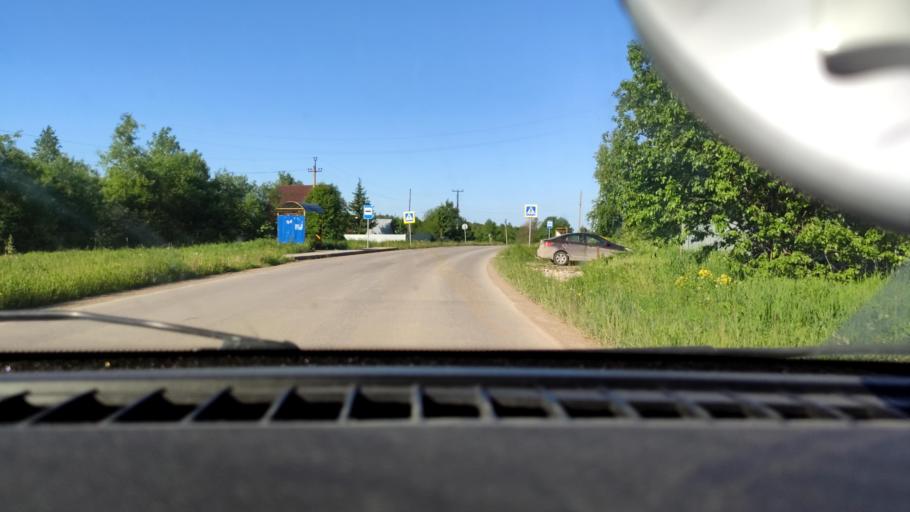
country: RU
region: Perm
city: Polazna
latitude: 58.2066
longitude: 56.5010
